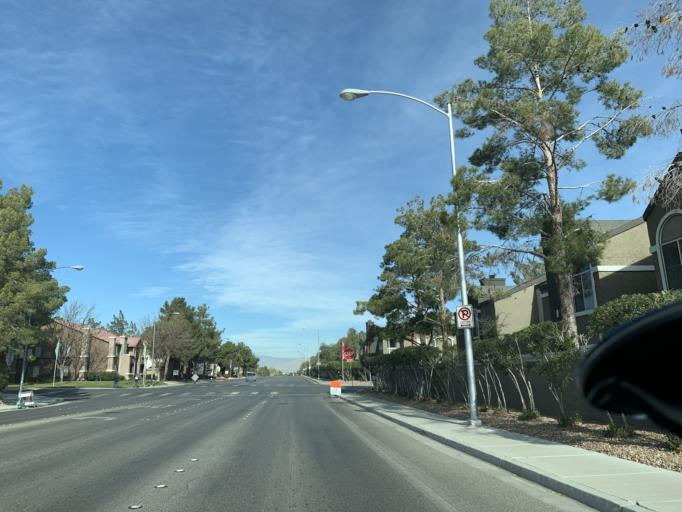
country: US
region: Nevada
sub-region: Clark County
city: Spring Valley
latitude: 36.0962
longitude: -115.2165
